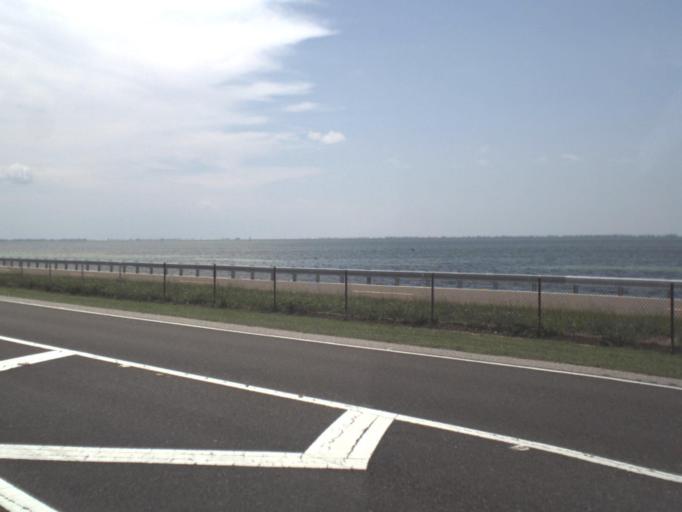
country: US
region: Florida
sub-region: Pinellas County
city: Tierra Verde
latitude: 27.6463
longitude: -82.6735
